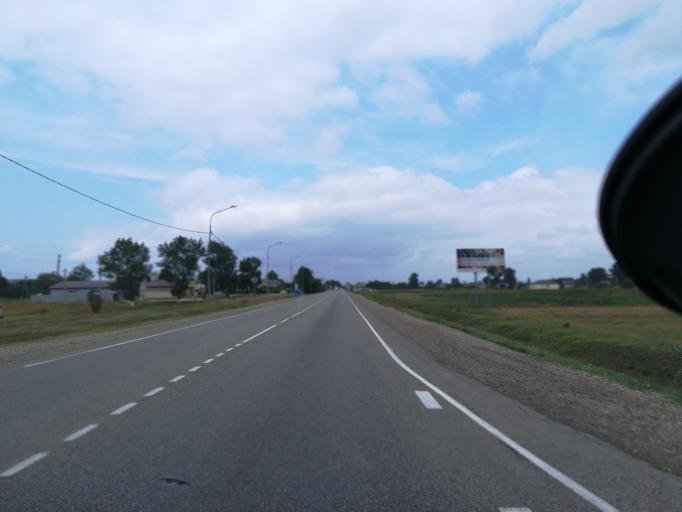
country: RU
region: Krasnodarskiy
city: Korzhevskiy
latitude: 45.1962
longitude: 37.6709
